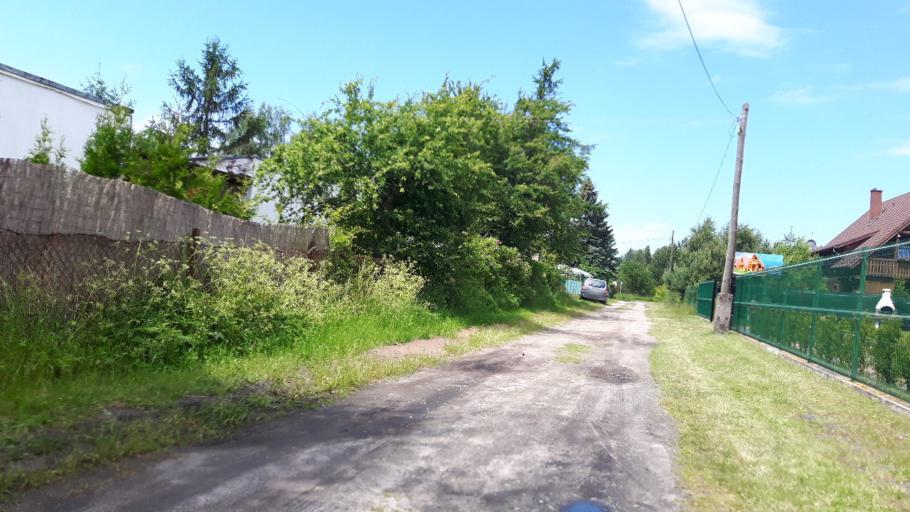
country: PL
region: West Pomeranian Voivodeship
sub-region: Powiat gryficki
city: Mrzezyno
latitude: 54.1408
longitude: 15.3009
